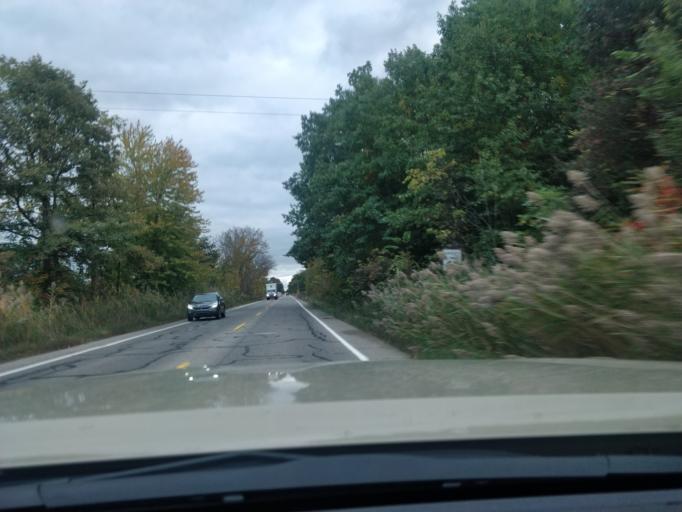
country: US
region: Michigan
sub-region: Wayne County
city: Romulus
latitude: 42.1805
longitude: -83.3503
